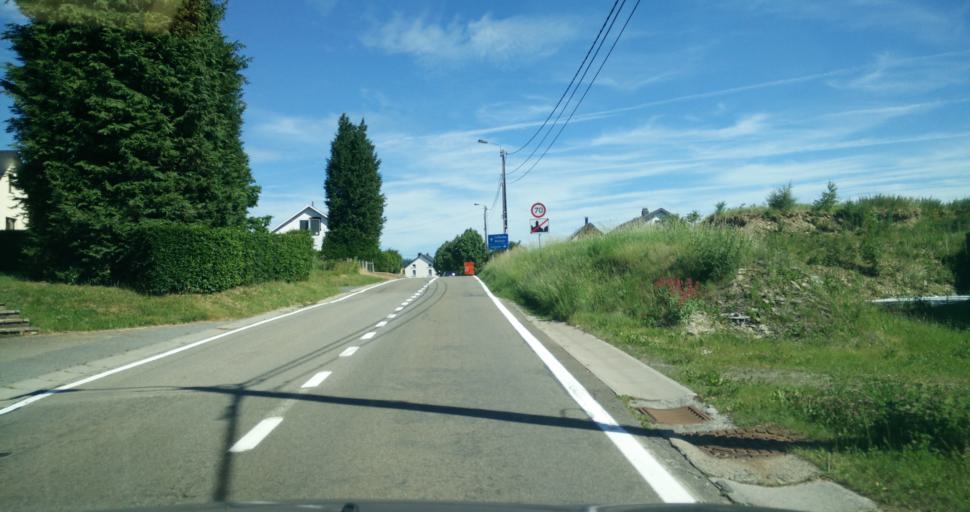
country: BE
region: Wallonia
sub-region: Province du Luxembourg
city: Bertogne
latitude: 50.1641
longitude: 5.6775
